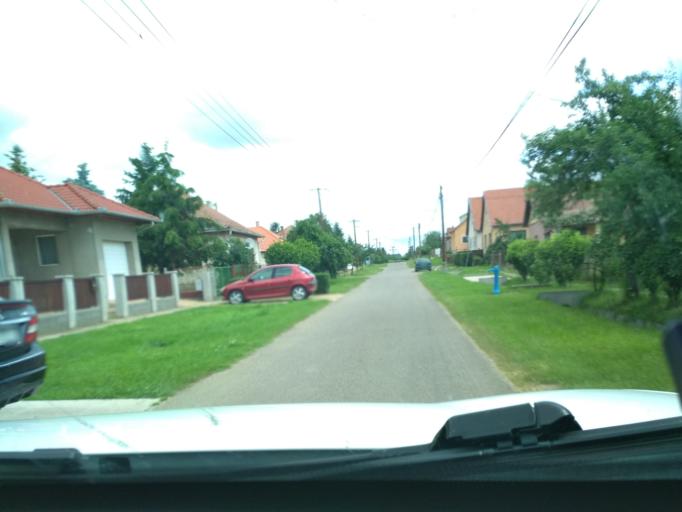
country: HU
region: Jasz-Nagykun-Szolnok
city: Tiszafured
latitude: 47.6042
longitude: 20.7233
